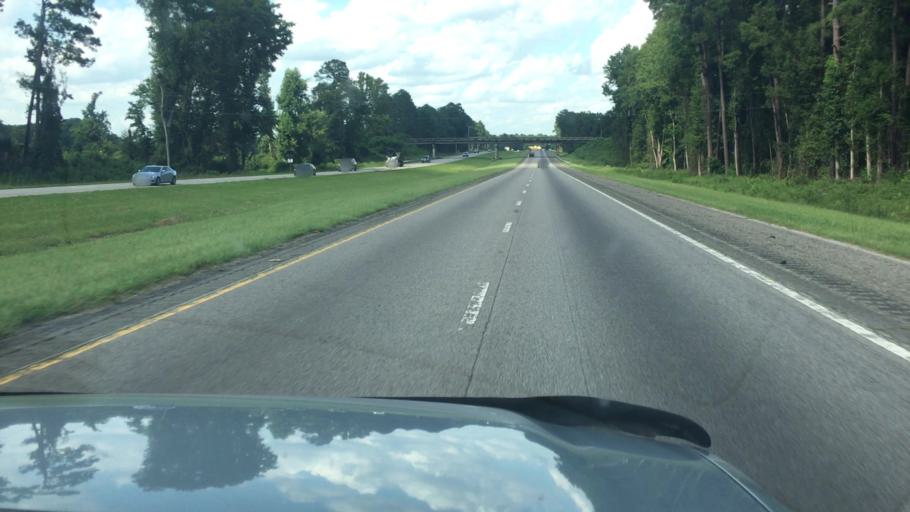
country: US
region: North Carolina
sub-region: Robeson County
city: Rowland
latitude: 34.4836
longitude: -79.3357
